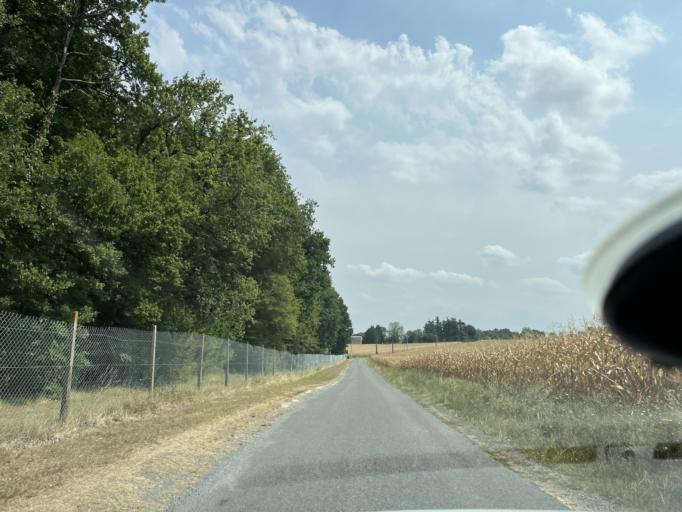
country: FR
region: Poitou-Charentes
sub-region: Departement de la Charente-Maritime
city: Pons
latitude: 45.6003
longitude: -0.5880
